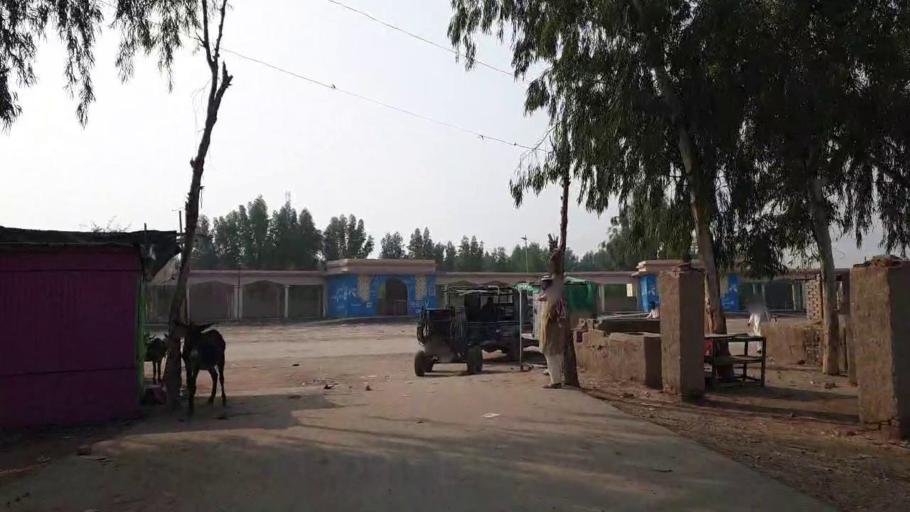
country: PK
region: Sindh
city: Sehwan
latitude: 26.4273
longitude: 67.8545
